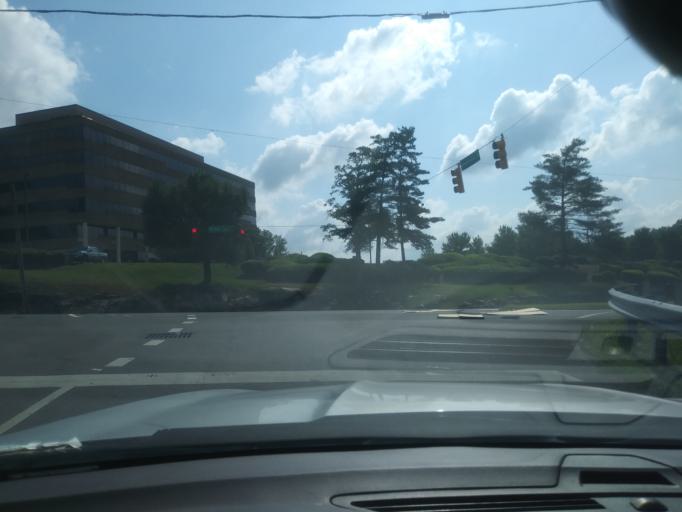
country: US
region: Tennessee
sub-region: Davidson County
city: Nashville
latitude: 36.1371
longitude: -86.6999
